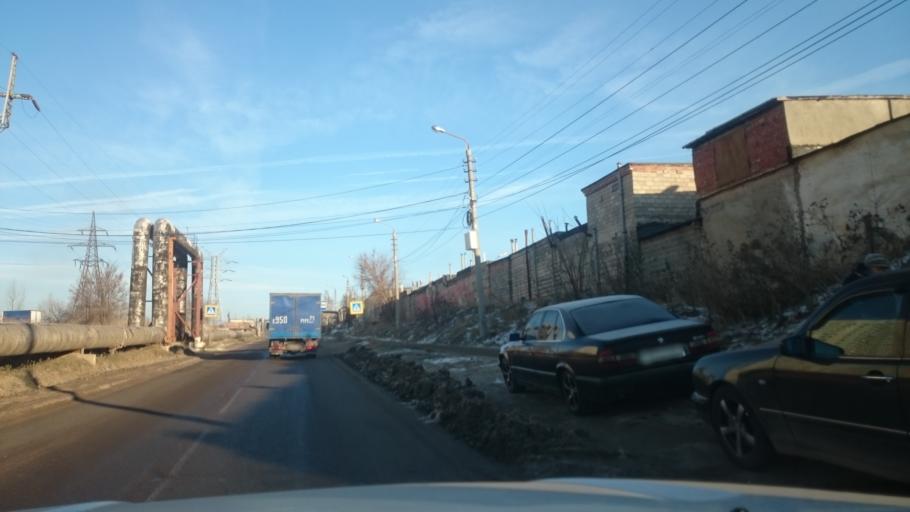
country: RU
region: Tula
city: Tula
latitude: 54.2131
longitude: 37.6857
